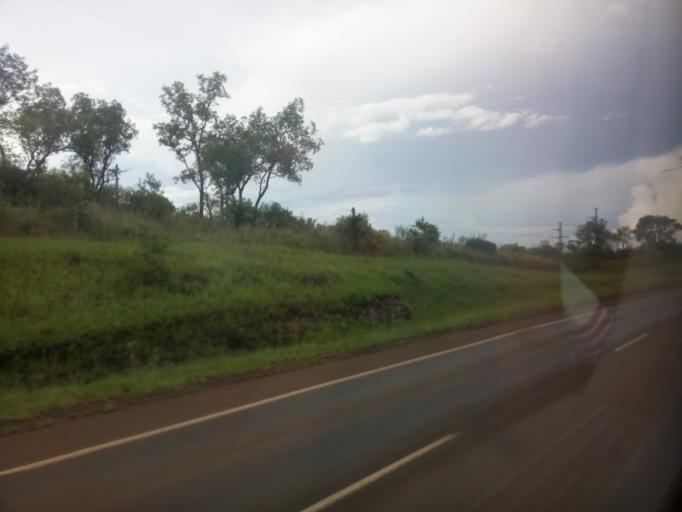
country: AR
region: Misiones
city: Santa Ana
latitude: -27.3971
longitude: -55.6019
